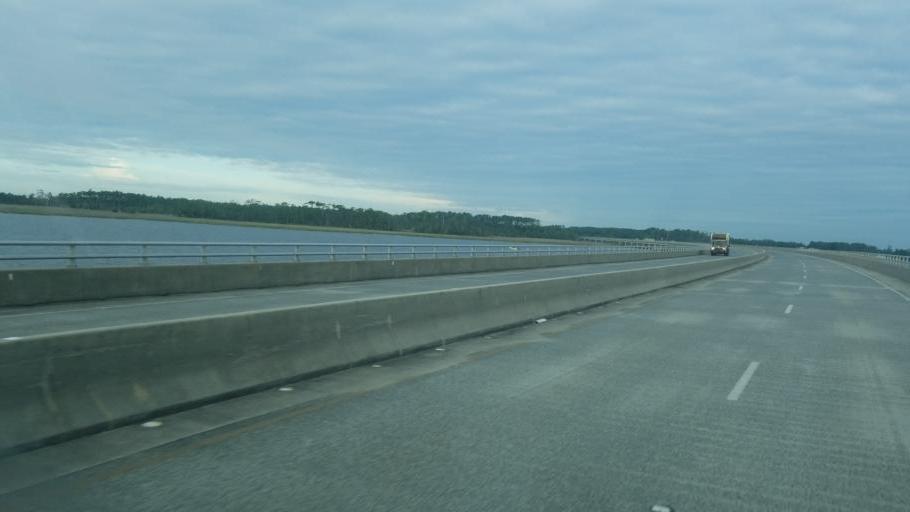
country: US
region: North Carolina
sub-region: Dare County
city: Manteo
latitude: 35.8886
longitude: -75.7477
